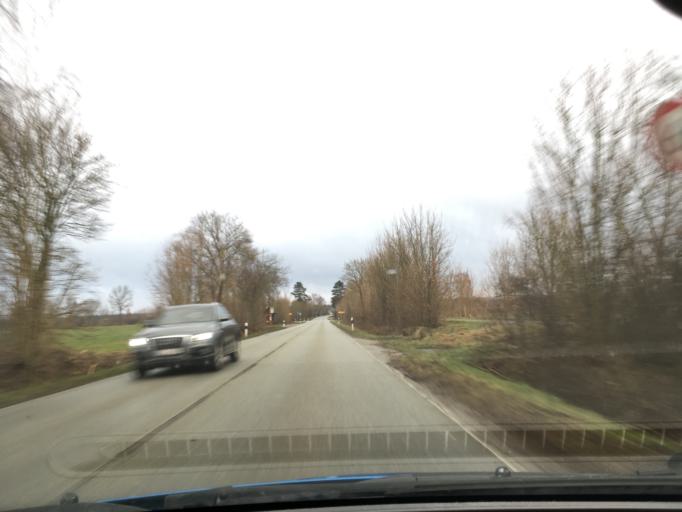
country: DE
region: Schleswig-Holstein
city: Siebeneichen
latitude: 53.5079
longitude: 10.6132
